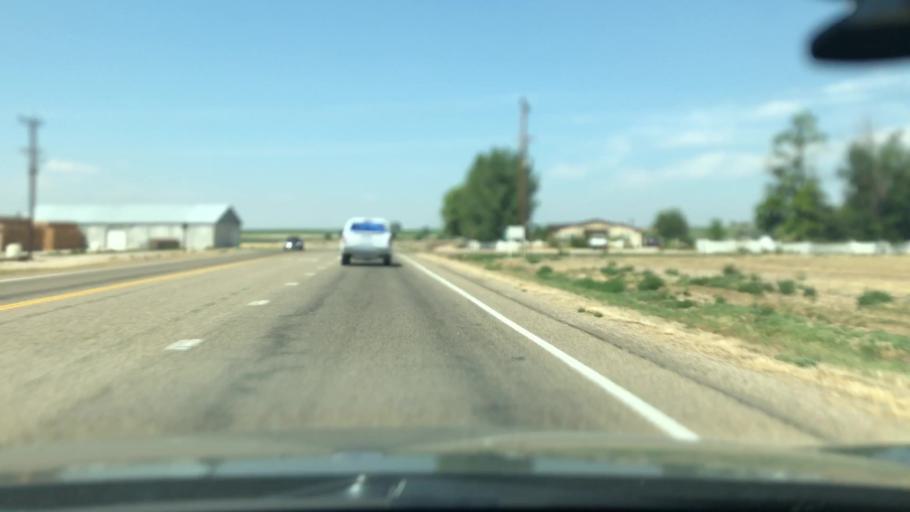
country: US
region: Idaho
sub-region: Canyon County
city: Parma
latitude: 43.8065
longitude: -116.9533
